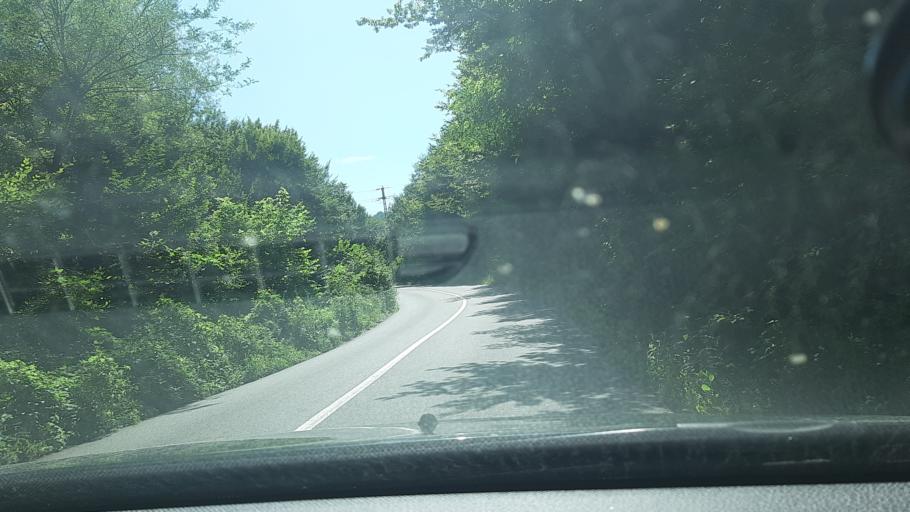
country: RO
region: Hunedoara
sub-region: Comuna Teliucu Inferior
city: Teliucu Inferior
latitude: 45.7017
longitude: 22.8810
